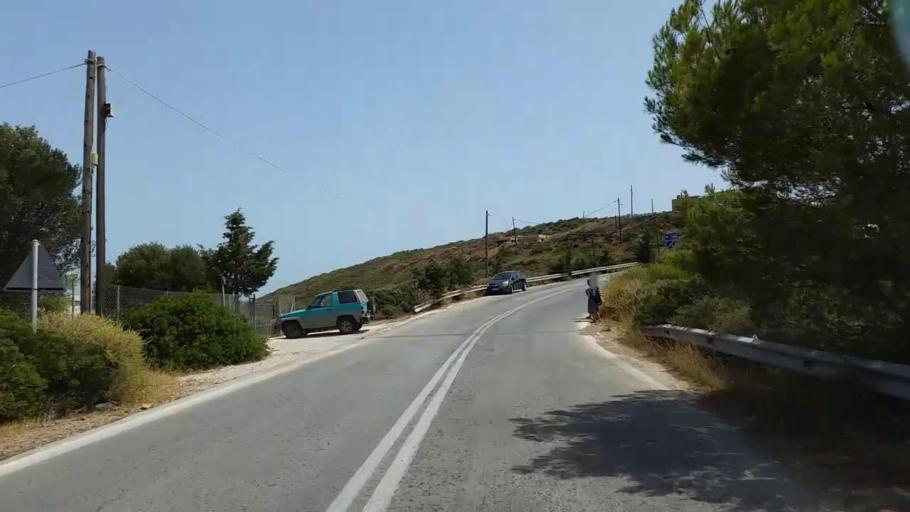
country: GR
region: Attica
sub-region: Nomarchia Anatolikis Attikis
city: Lavrio
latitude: 37.6525
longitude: 24.0266
